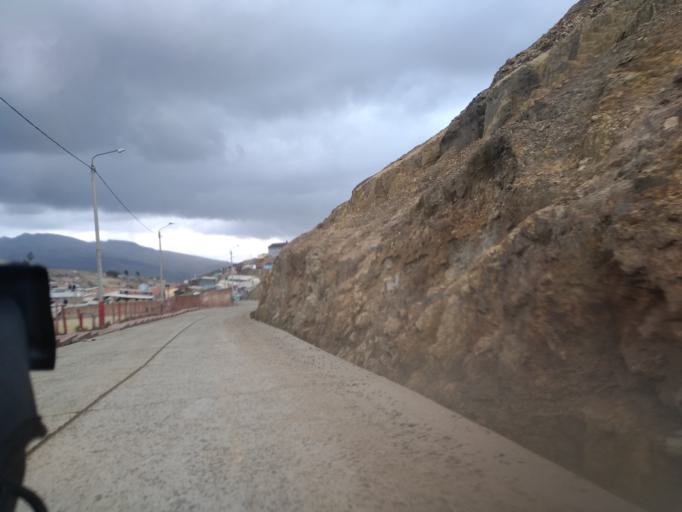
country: PE
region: La Libertad
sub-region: Provincia de Santiago de Chuco
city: Quiruvilca
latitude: -8.0006
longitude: -78.3079
